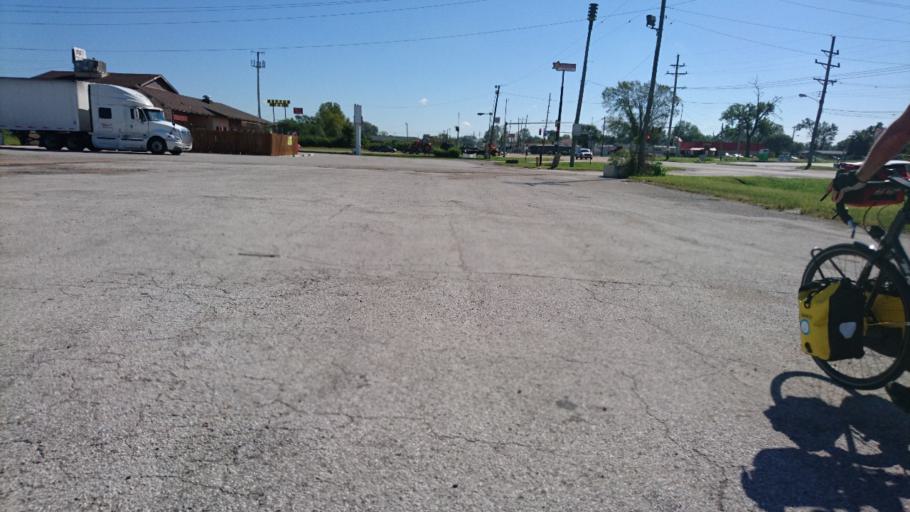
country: US
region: Illinois
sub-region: Madison County
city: Mitchell
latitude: 38.7624
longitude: -90.1260
